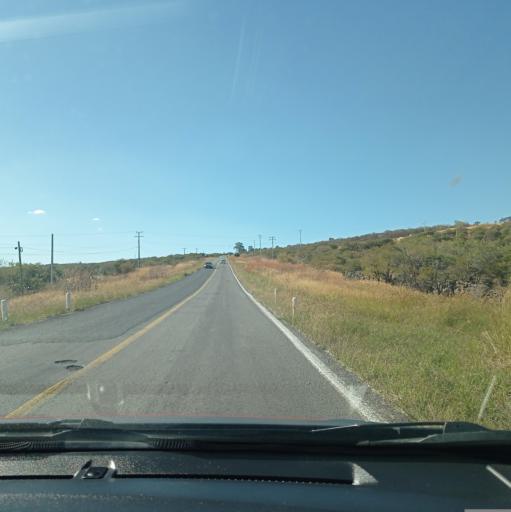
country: MX
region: Jalisco
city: Valle de Guadalupe
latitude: 21.0183
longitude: -102.5162
